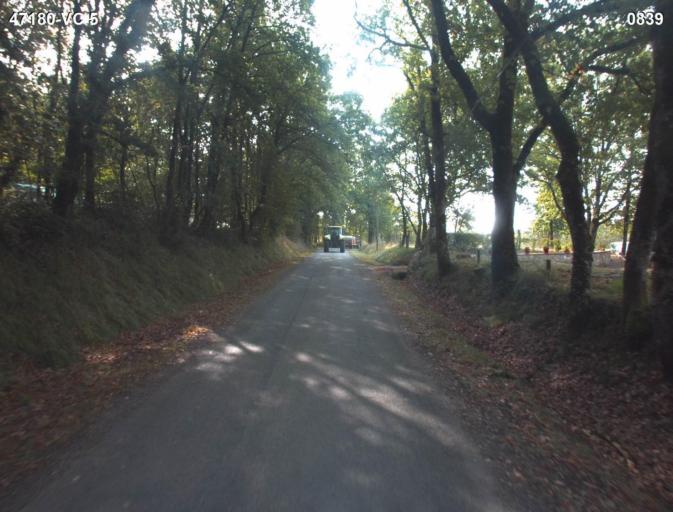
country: FR
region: Aquitaine
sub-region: Departement du Lot-et-Garonne
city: Sainte-Colombe-en-Bruilhois
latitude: 44.1755
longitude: 0.4683
